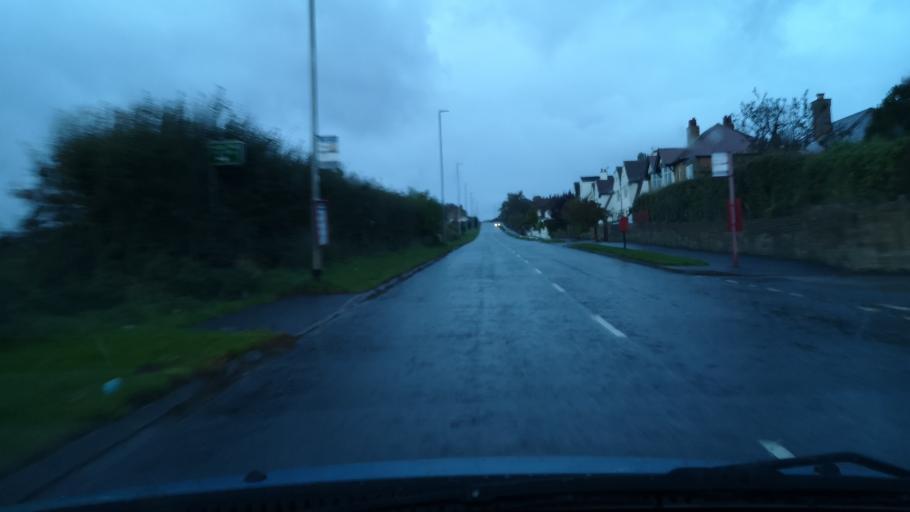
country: GB
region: England
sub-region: City and Borough of Leeds
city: Morley
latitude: 53.7306
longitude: -1.6193
